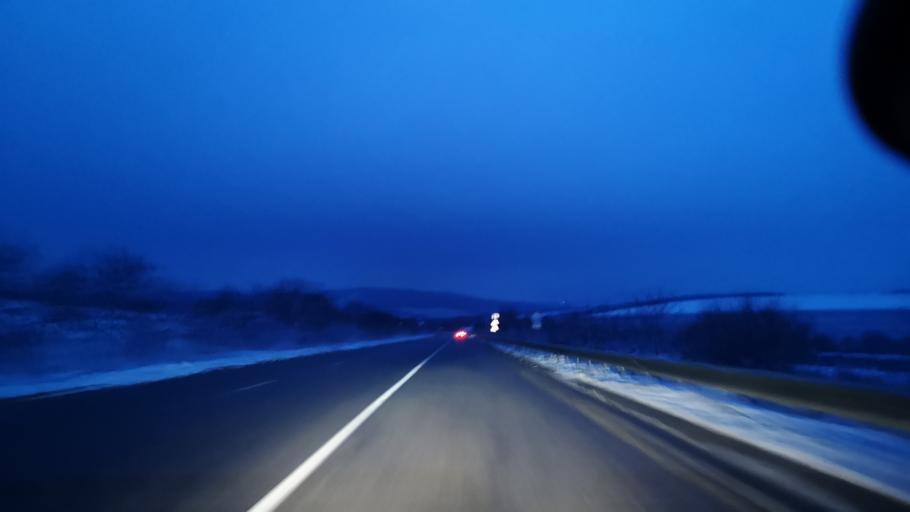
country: MD
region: Orhei
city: Orhei
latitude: 47.5278
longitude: 28.7957
